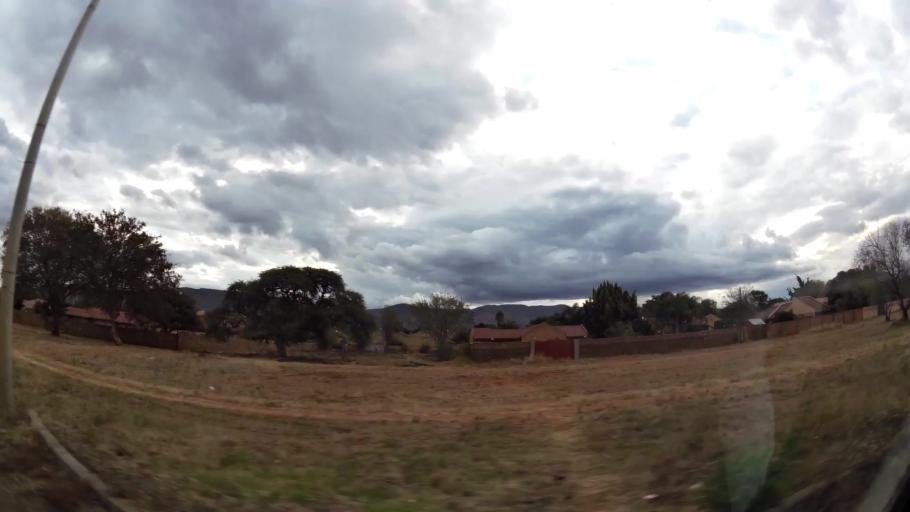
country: ZA
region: Limpopo
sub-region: Waterberg District Municipality
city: Mokopane
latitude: -24.2077
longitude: 29.0061
